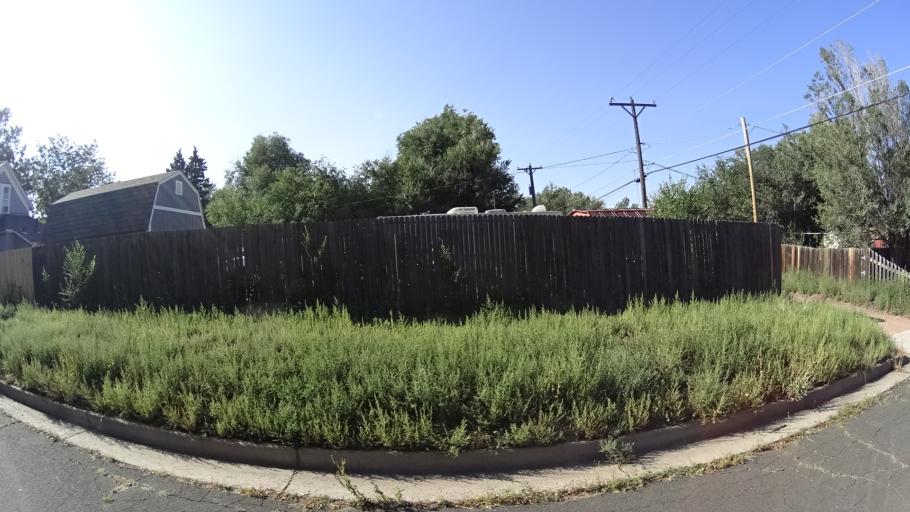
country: US
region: Colorado
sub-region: El Paso County
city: Colorado Springs
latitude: 38.8712
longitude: -104.8289
